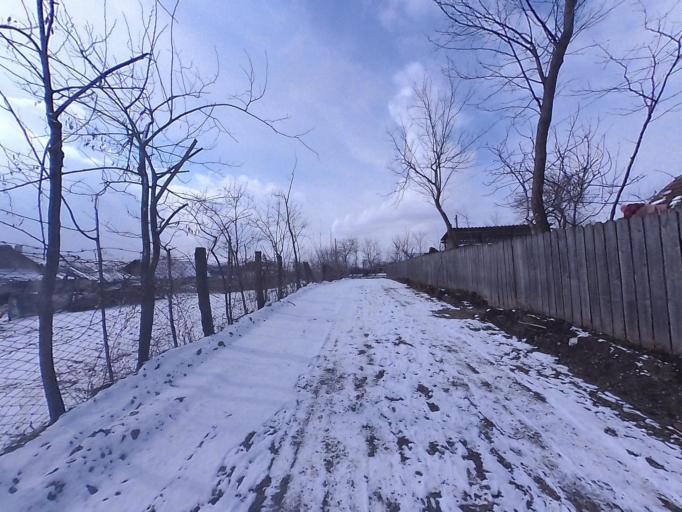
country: RO
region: Iasi
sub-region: Comuna Gropnita
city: Gropnita
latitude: 47.3594
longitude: 27.2505
